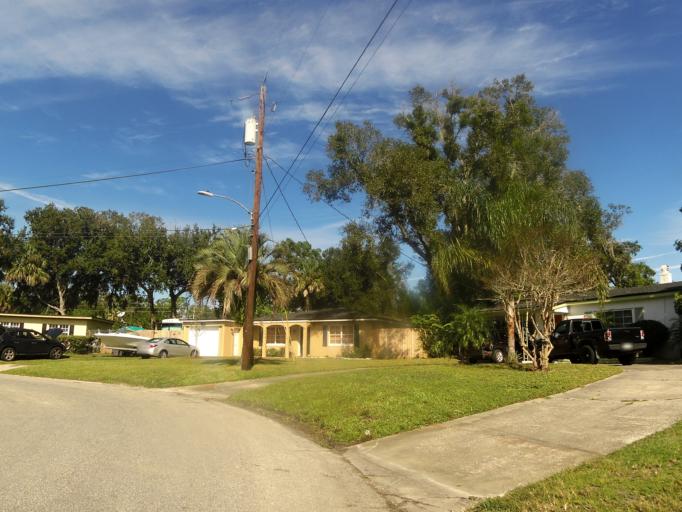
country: US
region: Florida
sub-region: Duval County
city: Jacksonville
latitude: 30.2599
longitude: -81.6358
